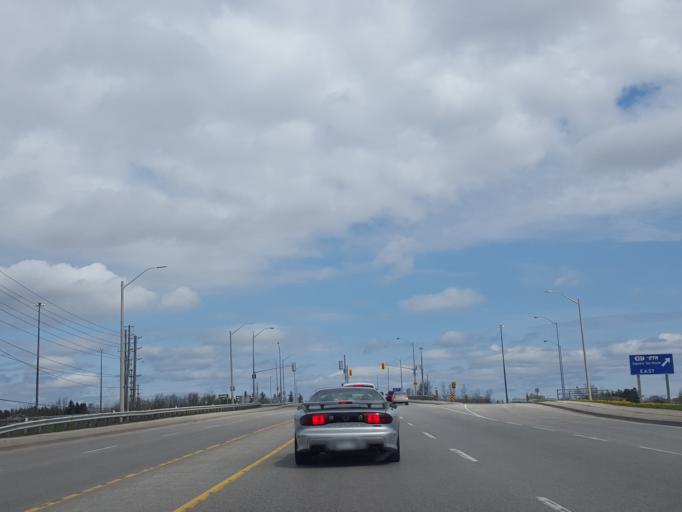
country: CA
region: Ontario
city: Markham
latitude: 43.8601
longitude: -79.2566
